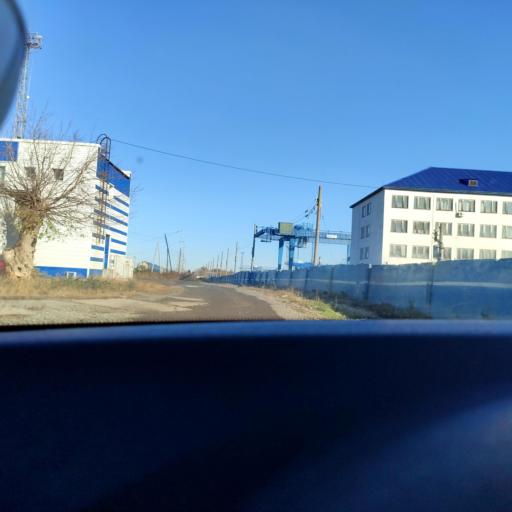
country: RU
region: Samara
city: Samara
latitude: 53.2034
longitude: 50.2482
